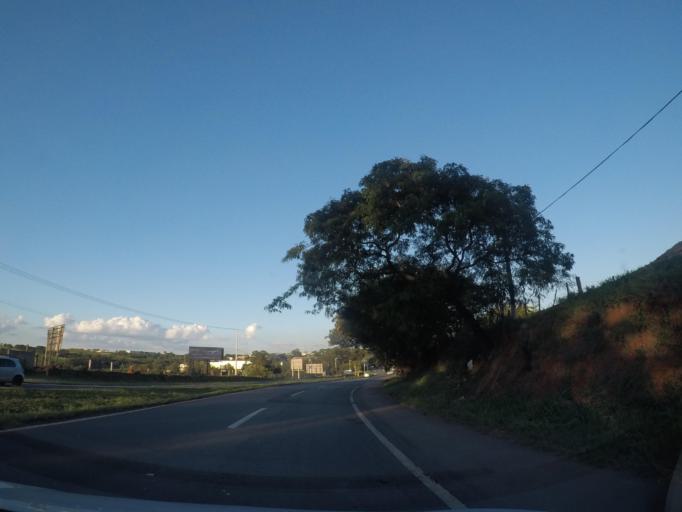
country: BR
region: Sao Paulo
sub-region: Sumare
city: Sumare
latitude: -22.8003
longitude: -47.2367
